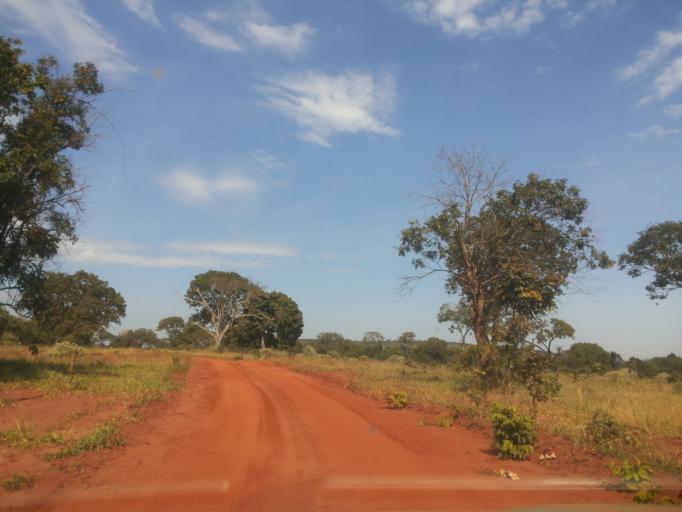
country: BR
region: Minas Gerais
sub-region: Ituiutaba
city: Ituiutaba
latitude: -19.0584
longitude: -49.3641
